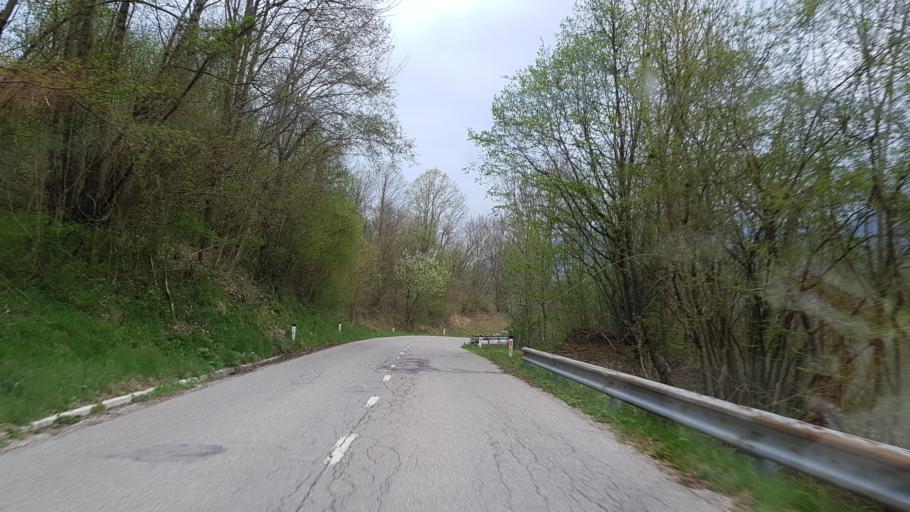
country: IT
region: Friuli Venezia Giulia
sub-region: Provincia di Udine
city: Pulfero
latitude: 46.2556
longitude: 13.4665
